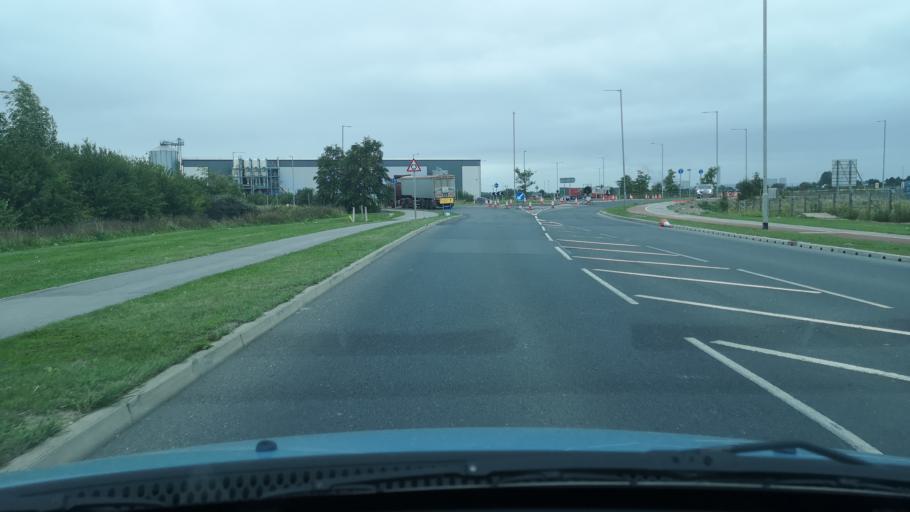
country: GB
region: England
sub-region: East Riding of Yorkshire
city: Airmyn
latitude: 53.7000
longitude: -0.9039
